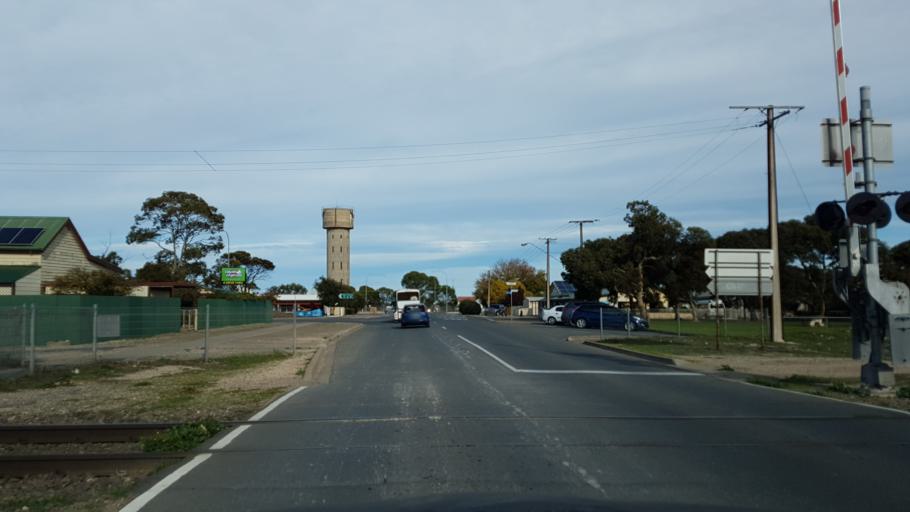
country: AU
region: South Australia
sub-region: Murray Bridge
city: Tailem Bend
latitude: -35.2525
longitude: 139.4541
